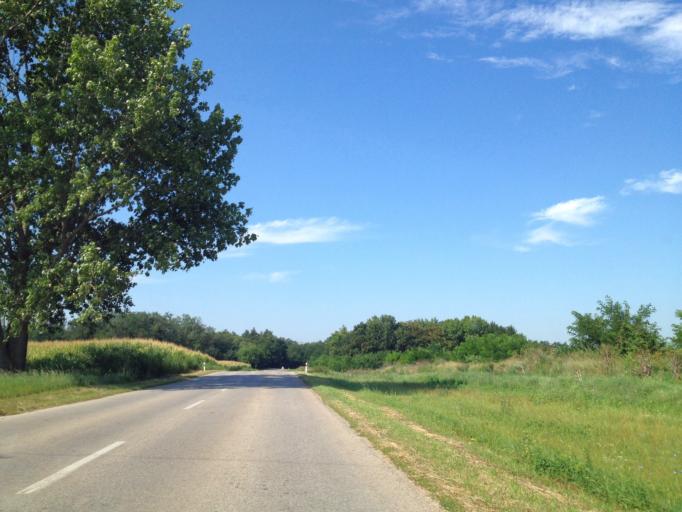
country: SK
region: Nitriansky
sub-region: Okres Komarno
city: Hurbanovo
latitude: 47.8362
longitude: 18.2477
